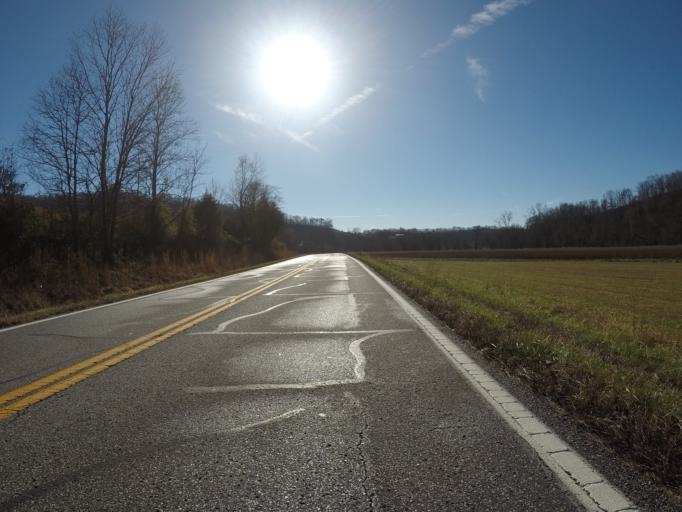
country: US
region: West Virginia
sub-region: Cabell County
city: Huntington
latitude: 38.4792
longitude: -82.4460
